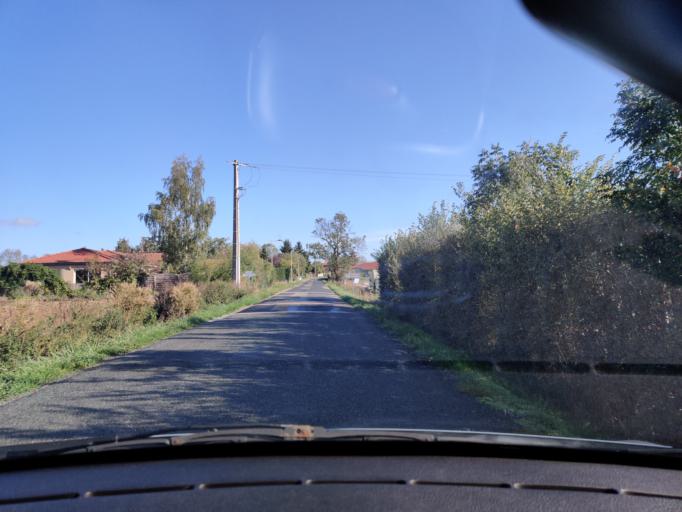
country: FR
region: Auvergne
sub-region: Departement du Puy-de-Dome
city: Combronde
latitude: 46.0366
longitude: 3.1233
